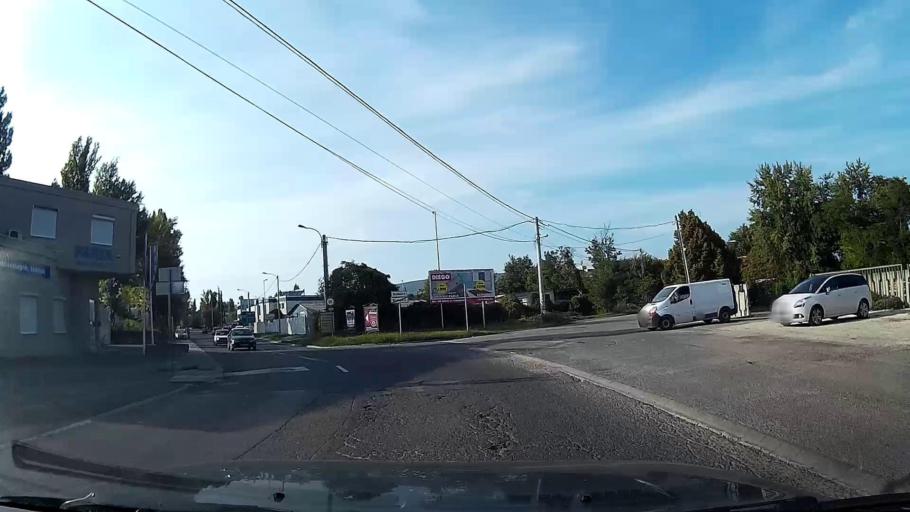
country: HU
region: Pest
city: Budaors
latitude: 47.4452
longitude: 18.9780
